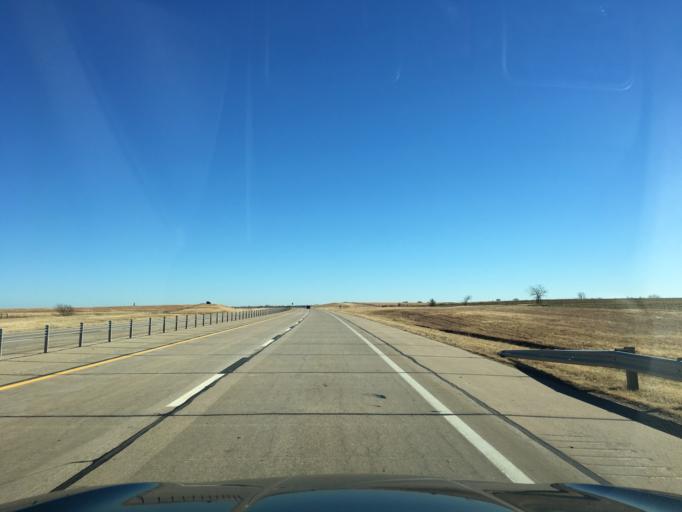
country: US
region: Oklahoma
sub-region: Noble County
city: Perry
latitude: 36.3954
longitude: -97.2235
